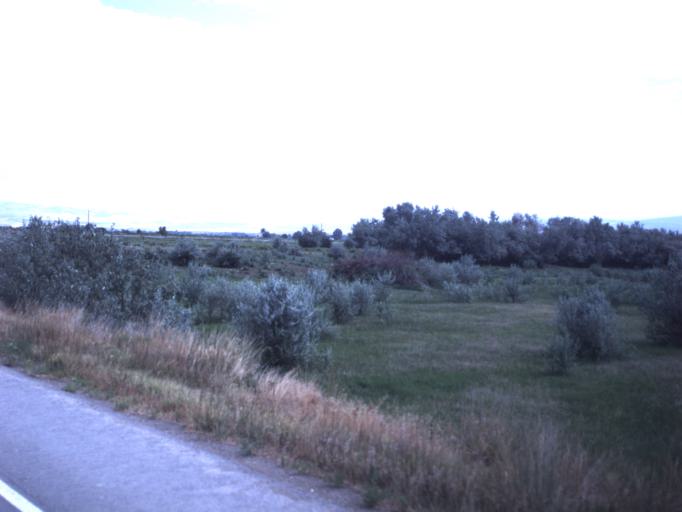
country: US
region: Utah
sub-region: Uintah County
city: Naples
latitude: 40.3795
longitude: -109.4985
